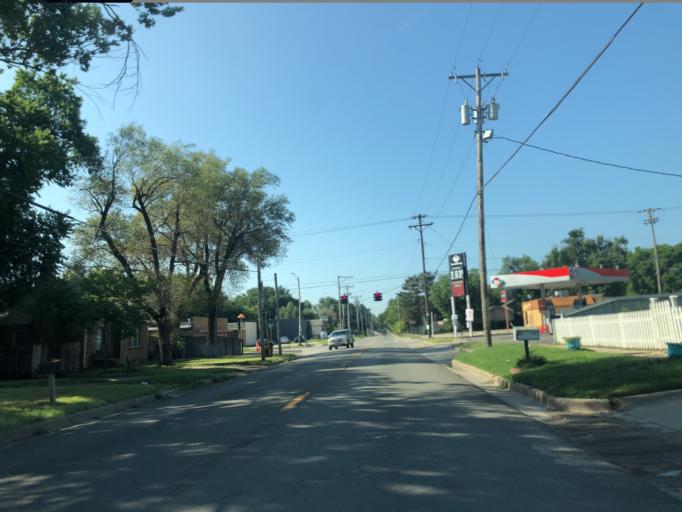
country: US
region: Kansas
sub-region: Sedgwick County
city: Wichita
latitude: 37.7384
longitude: -97.3449
